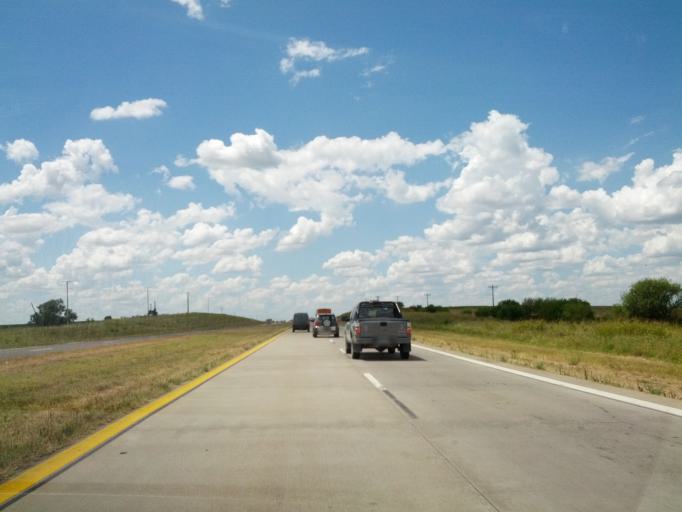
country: AR
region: Entre Rios
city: Gualeguaychu
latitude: -32.9156
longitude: -58.5637
